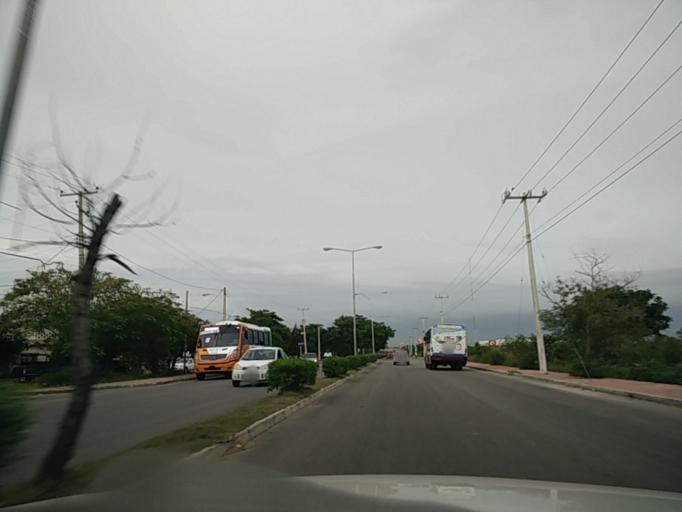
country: MX
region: Yucatan
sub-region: Kanasin
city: Kanasin
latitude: 20.9581
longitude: -89.5734
